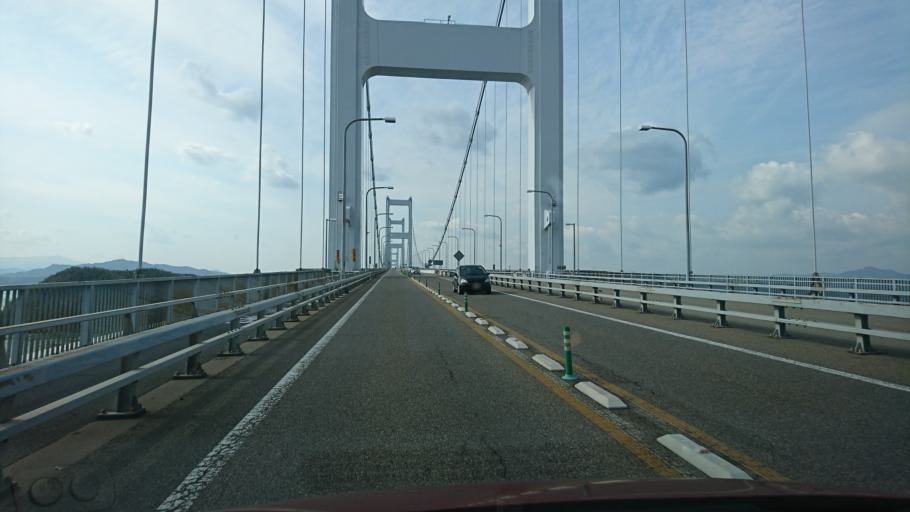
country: JP
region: Hiroshima
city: Innoshima
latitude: 34.1272
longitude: 133.0161
